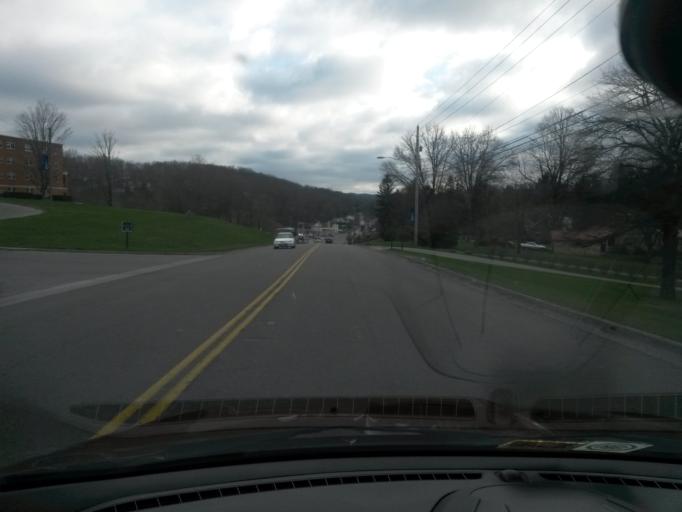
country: US
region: Virginia
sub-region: Tazewell County
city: Bluefield
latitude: 37.2440
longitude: -81.2453
